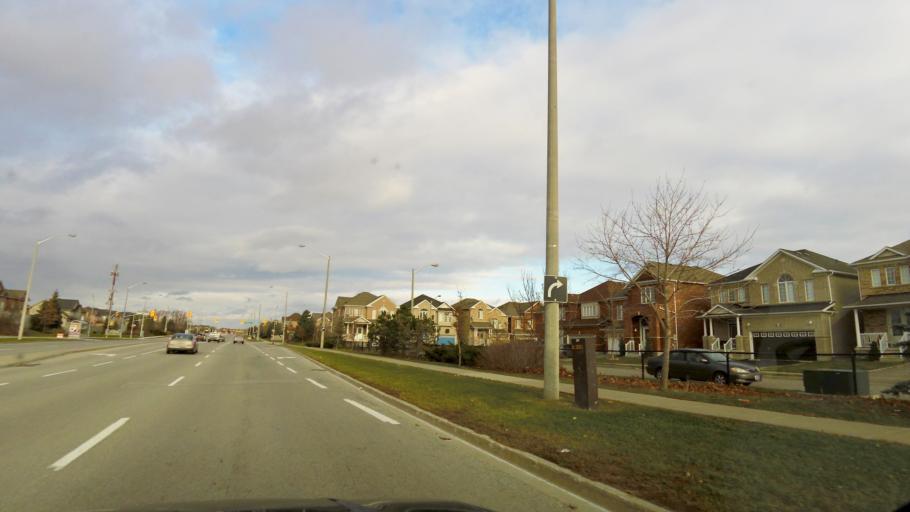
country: CA
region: Ontario
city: Brampton
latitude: 43.7758
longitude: -79.6784
